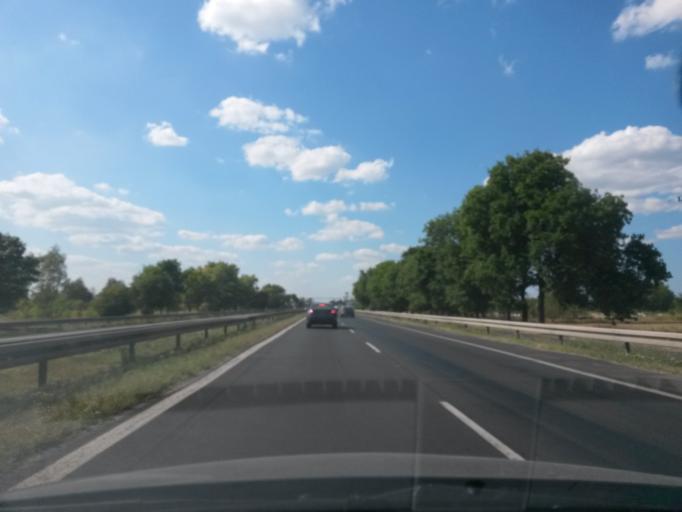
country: PL
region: Masovian Voivodeship
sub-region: Powiat warszawski zachodni
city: Dziekanow Lesny
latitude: 52.3559
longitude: 20.8406
